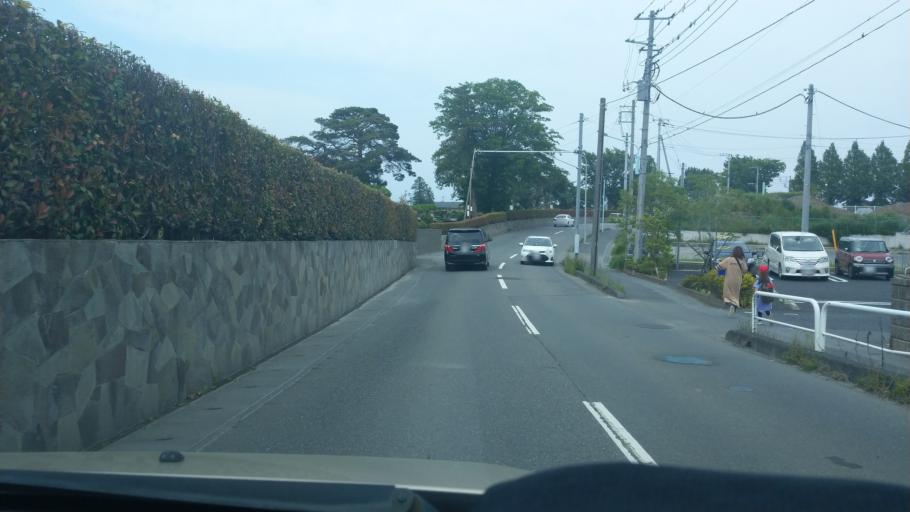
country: JP
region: Saitama
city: Yono
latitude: 35.9052
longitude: 139.5900
